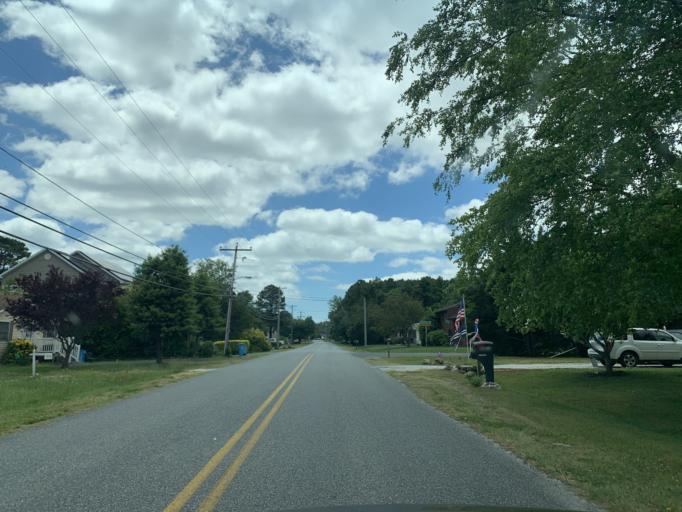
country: US
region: Maryland
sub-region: Worcester County
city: West Ocean City
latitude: 38.3521
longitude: -75.1177
